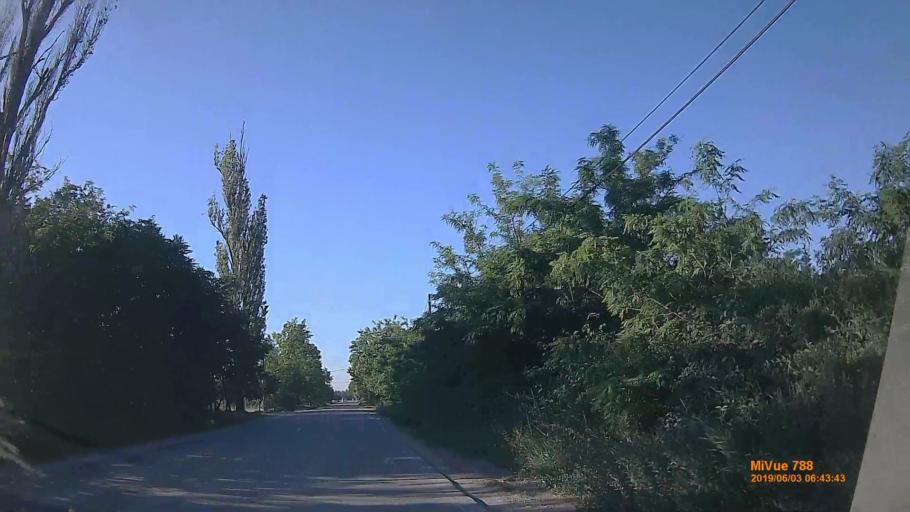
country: HU
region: Pest
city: Bugyi
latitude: 47.2520
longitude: 19.1266
